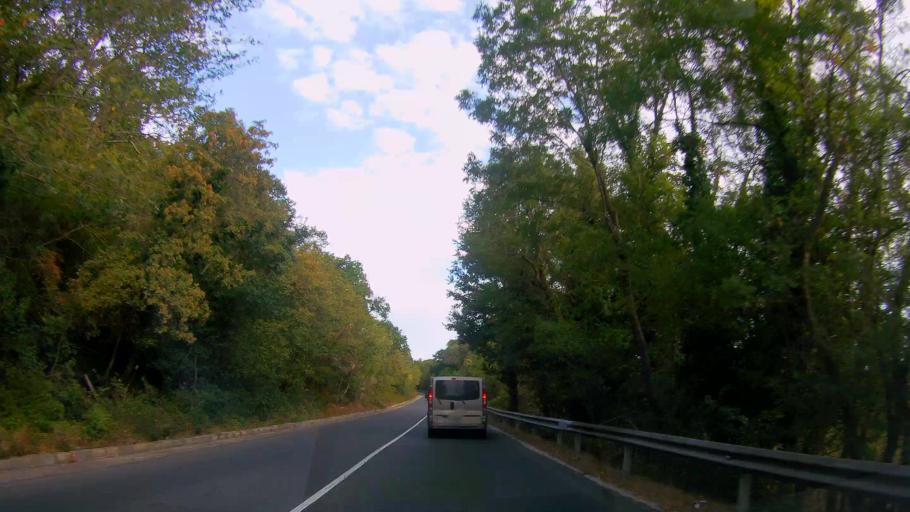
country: BG
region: Burgas
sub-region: Obshtina Primorsko
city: Primorsko
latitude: 42.3189
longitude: 27.7318
